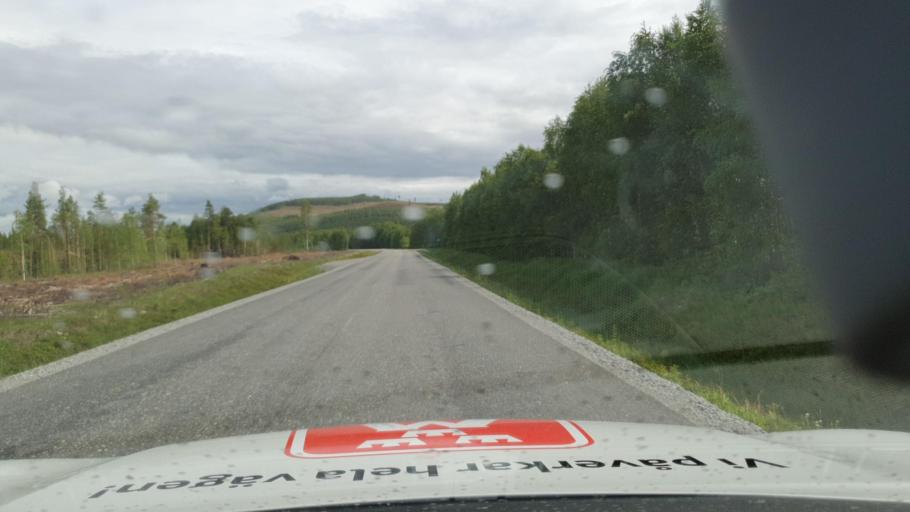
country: SE
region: Vaesterbotten
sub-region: Asele Kommun
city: Asele
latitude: 64.2069
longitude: 16.9401
